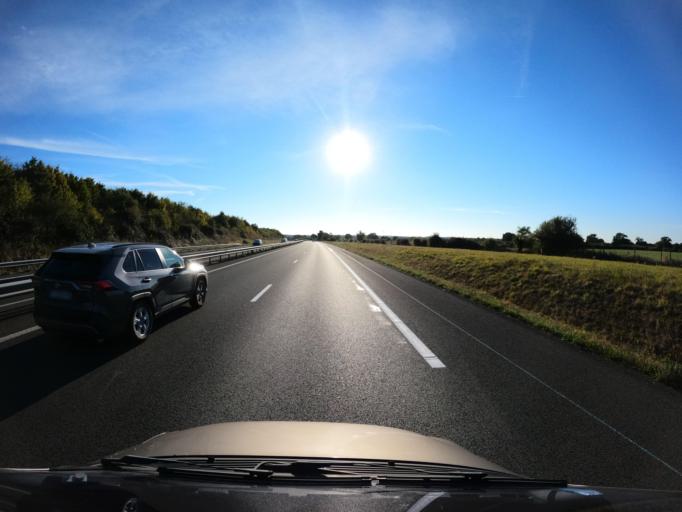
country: FR
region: Pays de la Loire
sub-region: Departement de Maine-et-Loire
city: Chemille-Melay
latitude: 47.2357
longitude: -0.7432
